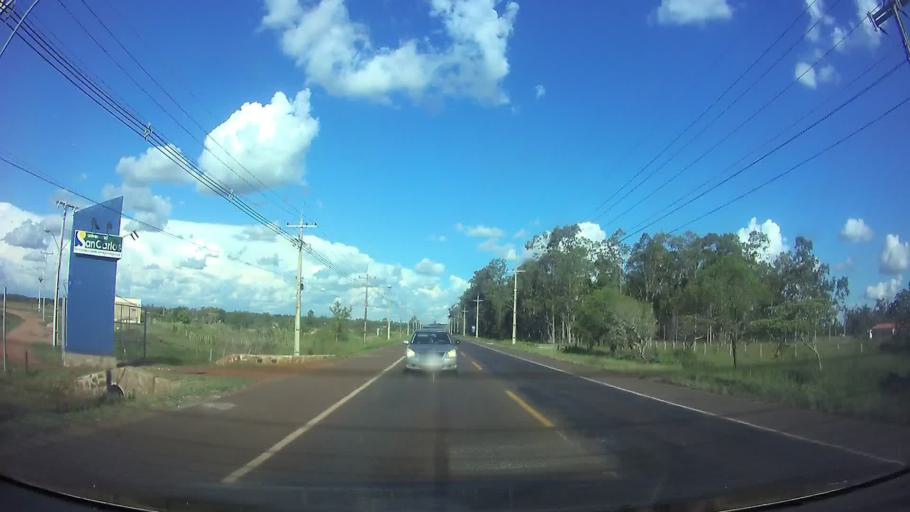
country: PY
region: Cordillera
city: Eusebio Ayala
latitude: -25.3808
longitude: -56.9829
